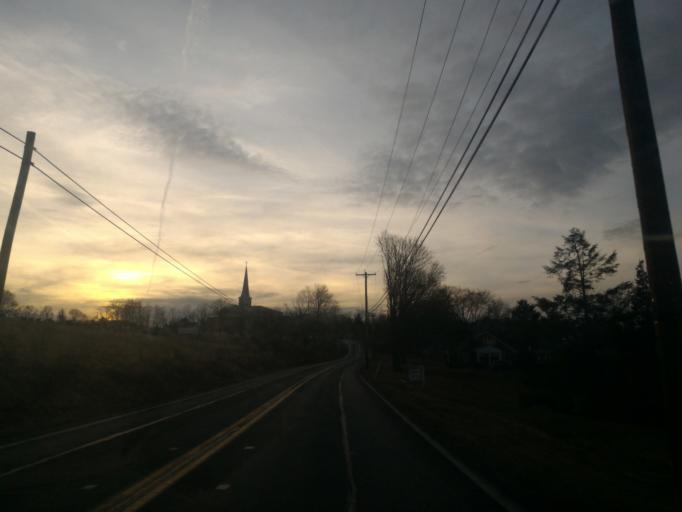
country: US
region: Pennsylvania
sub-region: York County
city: Jacobus
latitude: 39.8874
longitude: -76.7040
